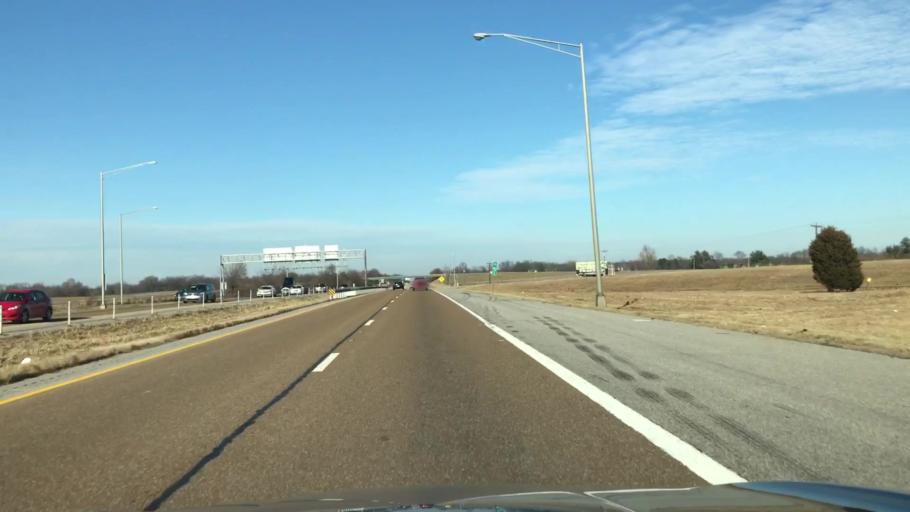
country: US
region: Illinois
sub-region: Madison County
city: Troy
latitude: 38.7535
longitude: -89.9067
